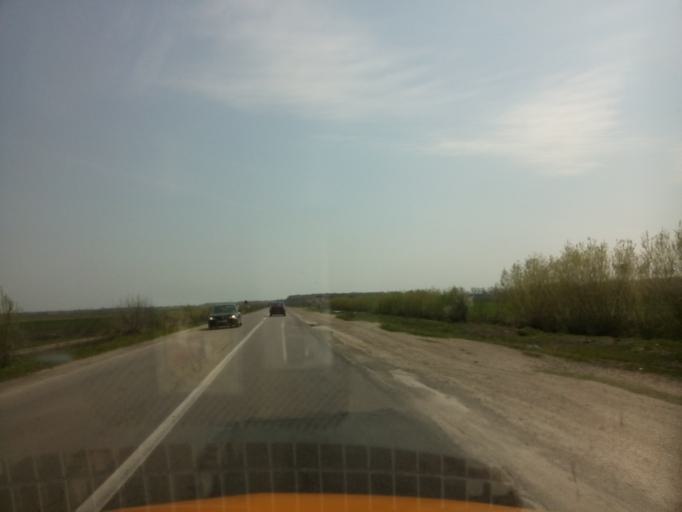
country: RO
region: Calarasi
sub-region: Comuna Crivat
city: Crivat
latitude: 44.2304
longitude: 26.4210
